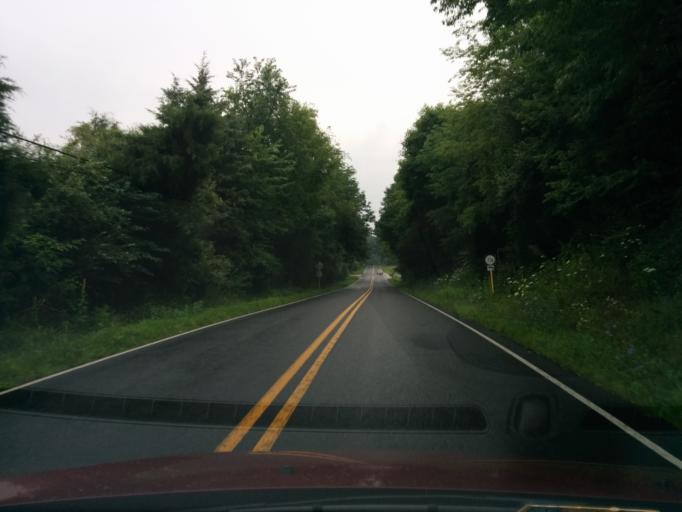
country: US
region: Virginia
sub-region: Rockbridge County
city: East Lexington
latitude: 37.8790
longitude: -79.3808
